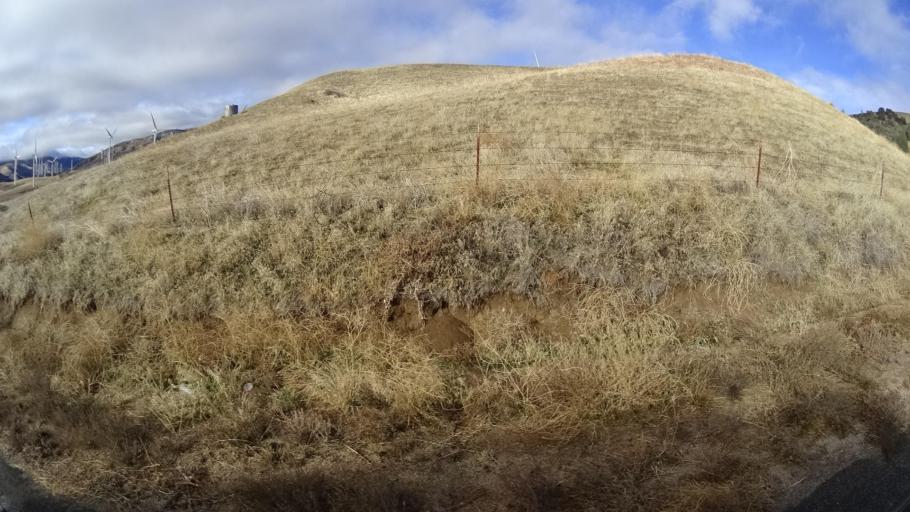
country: US
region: California
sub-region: Kern County
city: Tehachapi
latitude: 35.0668
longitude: -118.3507
